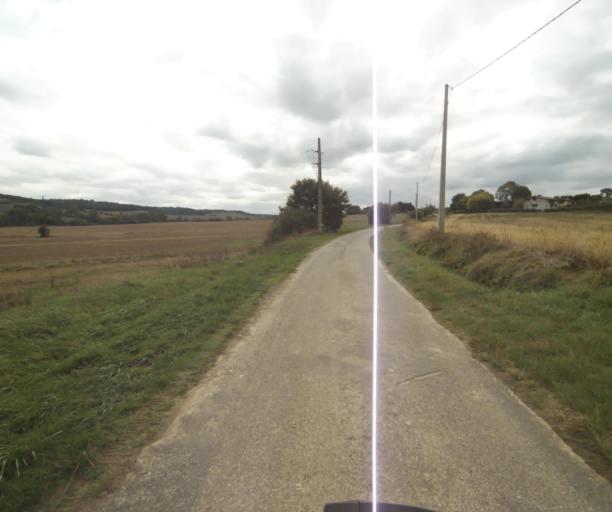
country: FR
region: Midi-Pyrenees
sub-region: Departement du Tarn-et-Garonne
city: Beaumont-de-Lomagne
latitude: 43.8260
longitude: 1.0886
